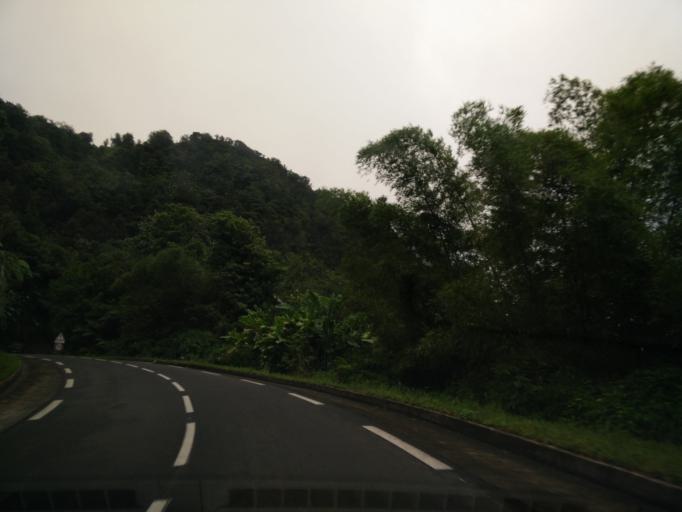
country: MQ
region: Martinique
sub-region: Martinique
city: Le Morne-Rouge
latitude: 14.7286
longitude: -61.1009
